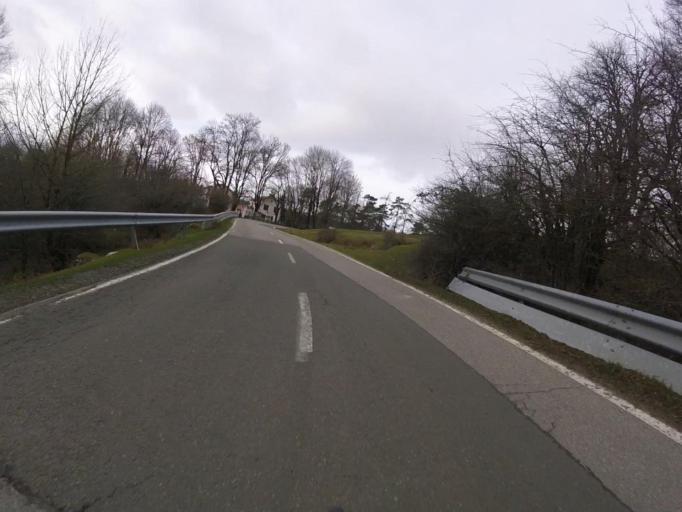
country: ES
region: Navarre
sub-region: Provincia de Navarra
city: Olazagutia
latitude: 42.8511
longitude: -2.1711
